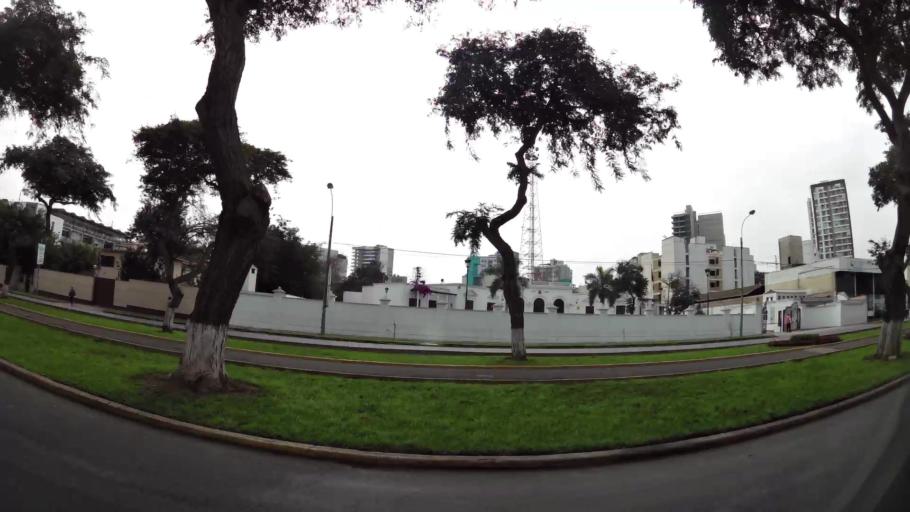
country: PE
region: Lima
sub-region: Lima
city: San Isidro
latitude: -12.0832
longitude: -77.0472
